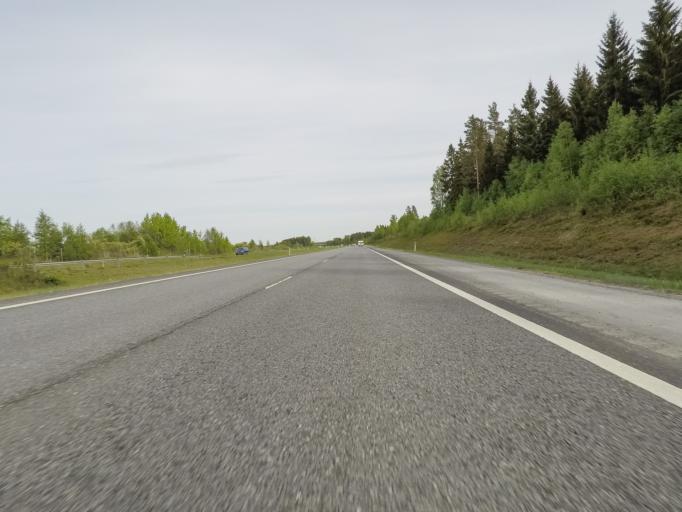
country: FI
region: Pirkanmaa
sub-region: Etelae-Pirkanmaa
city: Valkeakoski
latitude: 61.1478
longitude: 23.9985
